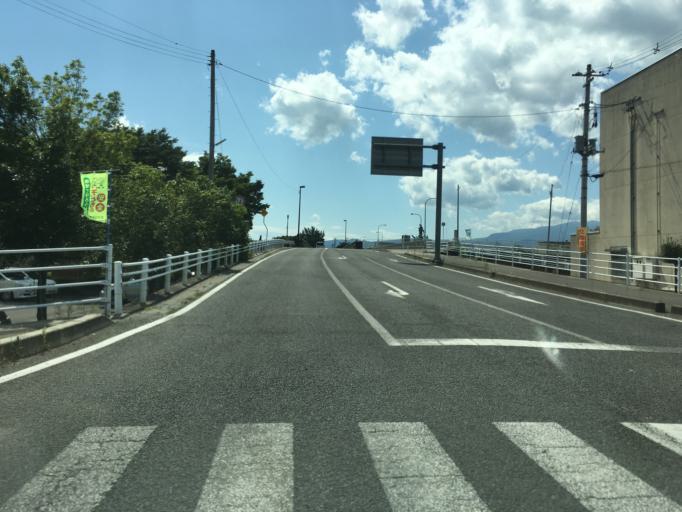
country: JP
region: Fukushima
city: Fukushima-shi
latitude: 37.7832
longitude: 140.4266
